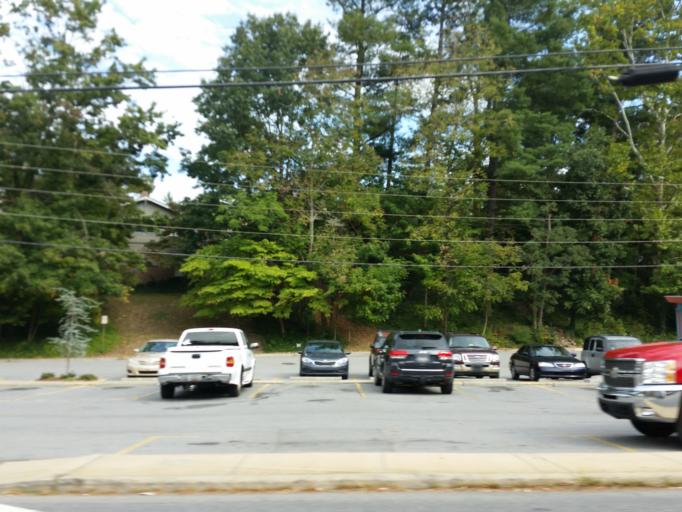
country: US
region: North Carolina
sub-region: Buncombe County
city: Asheville
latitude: 35.6156
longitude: -82.5548
